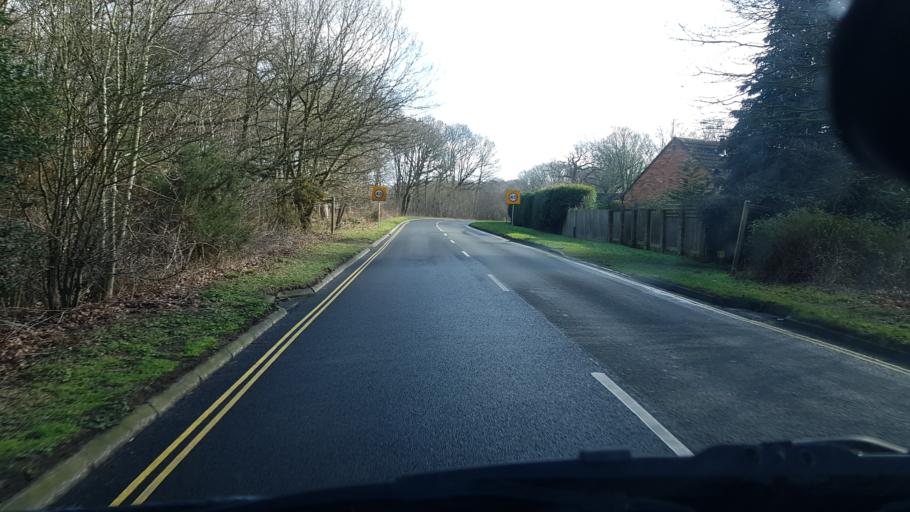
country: GB
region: England
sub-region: Surrey
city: Guildford
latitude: 51.2673
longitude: -0.5930
